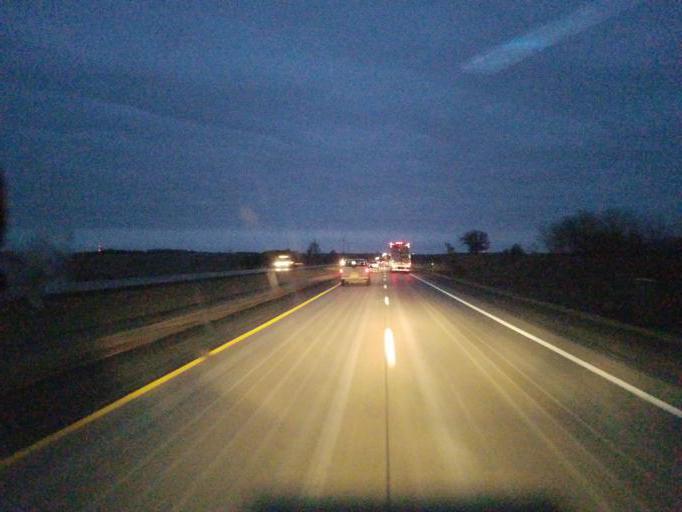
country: US
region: Iowa
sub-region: Guthrie County
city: Guthrie Center
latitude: 41.4966
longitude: -94.7317
